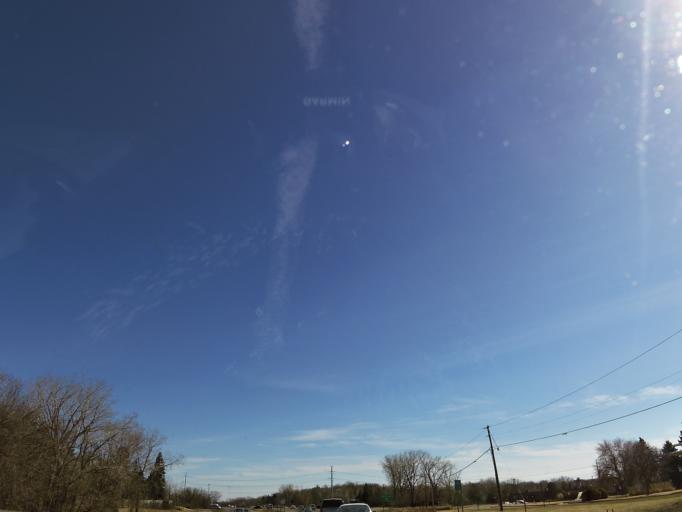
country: US
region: Minnesota
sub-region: Hennepin County
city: Plymouth
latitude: 44.9994
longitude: -93.4421
